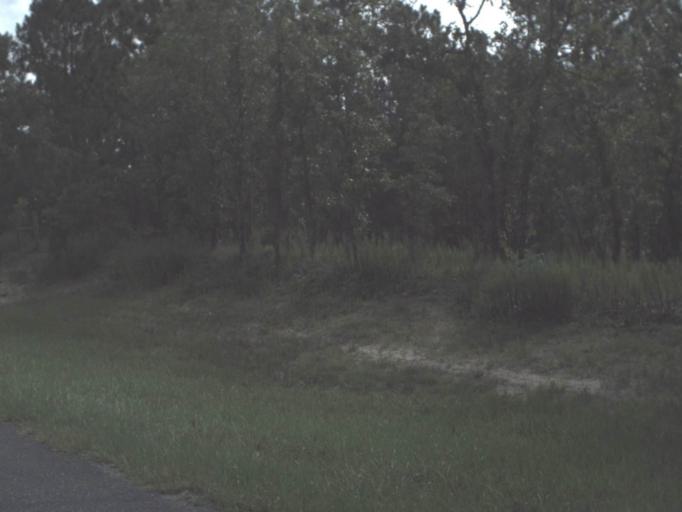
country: US
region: Florida
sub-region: Levy County
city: Williston Highlands
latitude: 29.3536
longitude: -82.5067
